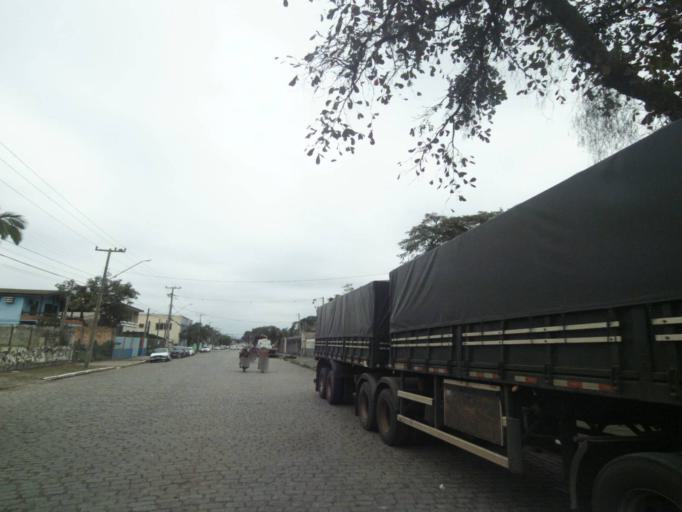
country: BR
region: Parana
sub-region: Paranagua
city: Paranagua
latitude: -25.5115
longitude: -48.5159
